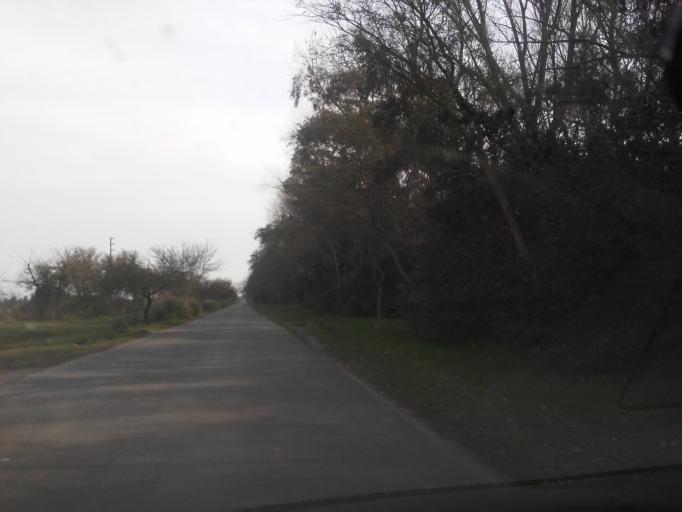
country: AR
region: Buenos Aires
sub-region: Partido de Marcos Paz
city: Marcos Paz
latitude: -34.6706
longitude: -58.8563
